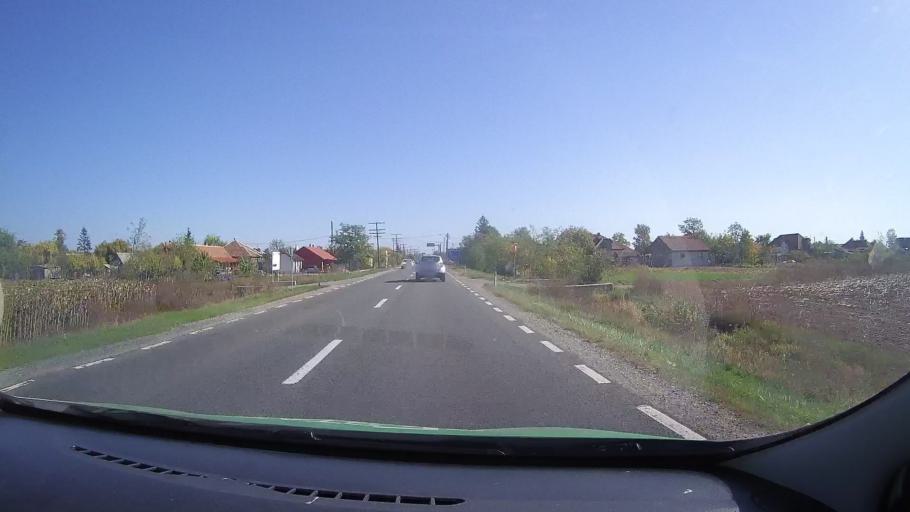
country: RO
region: Satu Mare
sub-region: Comuna Moftinu
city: Moftinu Mic
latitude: 47.6846
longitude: 22.5887
